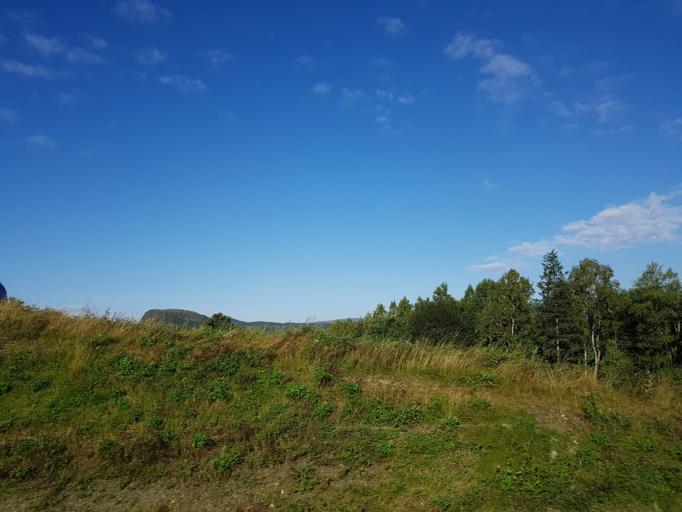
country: NO
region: Sor-Trondelag
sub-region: Trondheim
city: Trondheim
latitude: 63.6002
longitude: 10.2222
